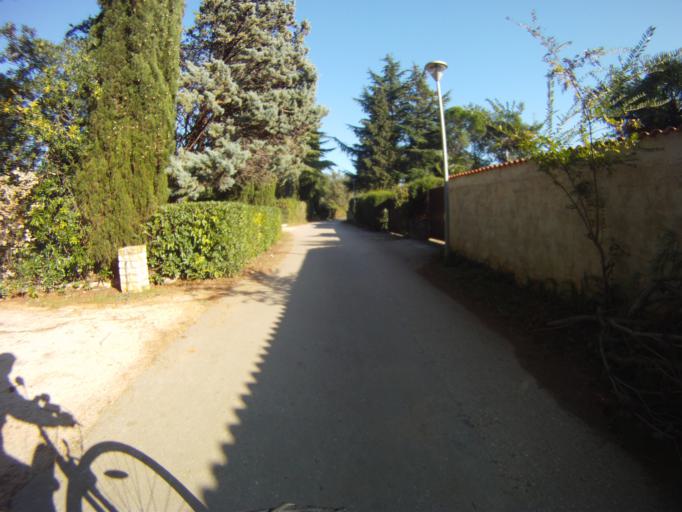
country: HR
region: Istarska
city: Umag
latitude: 45.4028
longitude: 13.5328
